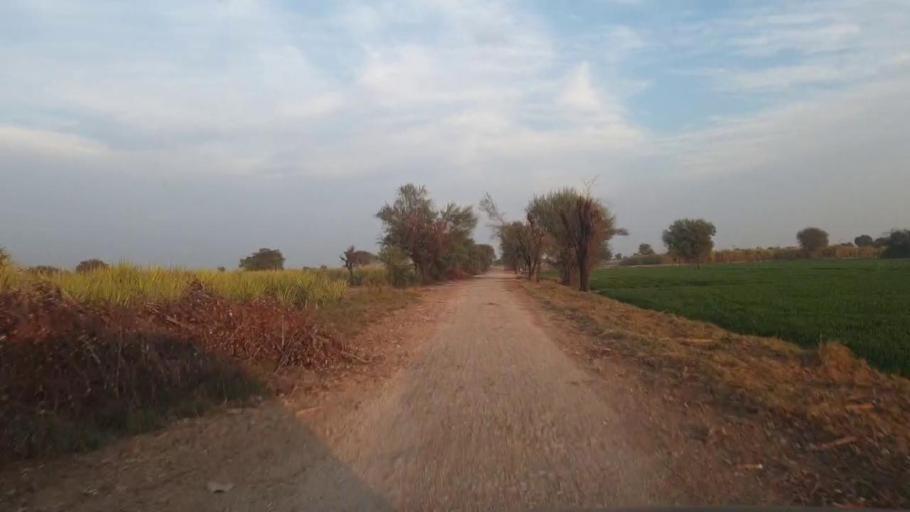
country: PK
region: Sindh
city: Shahpur Chakar
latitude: 26.0528
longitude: 68.5383
